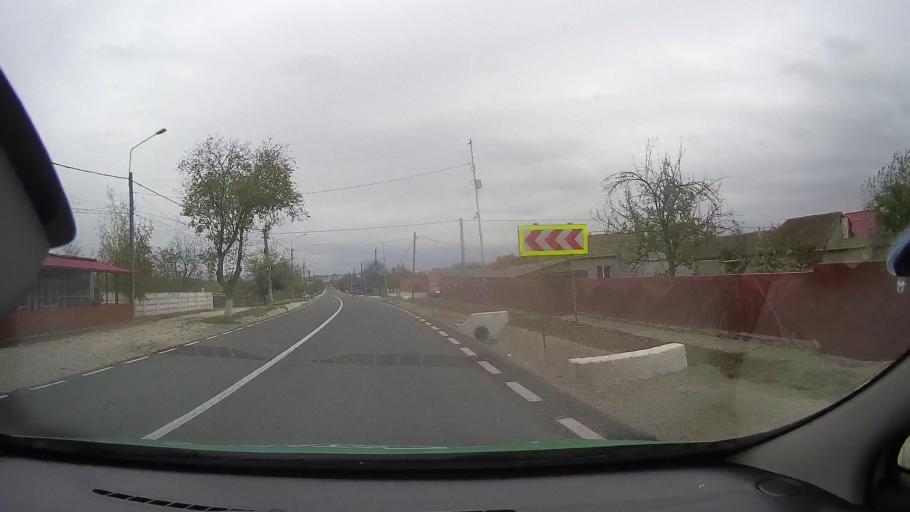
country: RO
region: Constanta
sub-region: Comuna Mihail Kogalniceanu
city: Mihail Kogalniceanu
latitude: 44.3677
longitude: 28.4537
